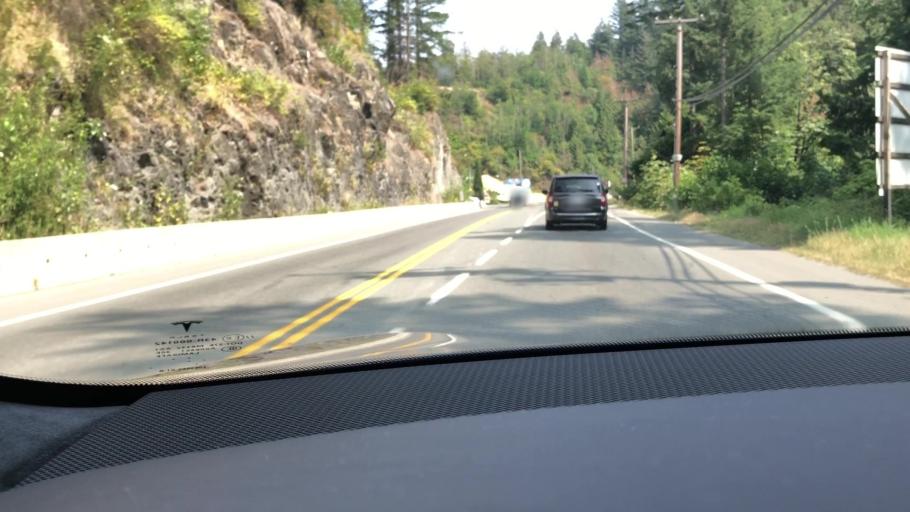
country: CA
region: British Columbia
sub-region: Fraser Valley Regional District
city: Chilliwack
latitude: 49.0923
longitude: -121.9702
